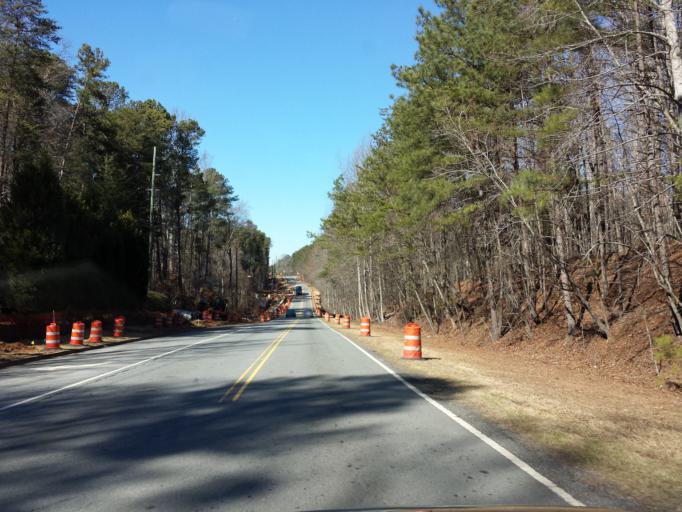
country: US
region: Georgia
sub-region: Cobb County
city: Marietta
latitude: 33.9400
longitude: -84.6053
